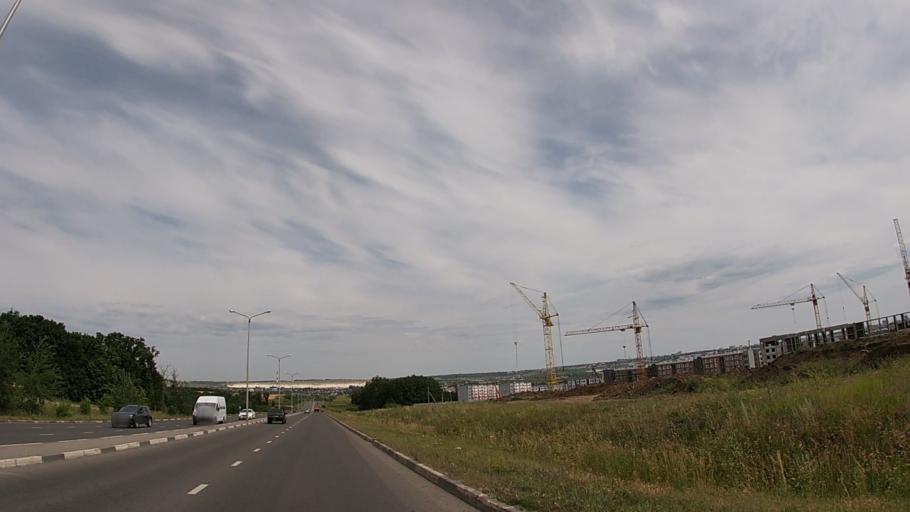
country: RU
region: Belgorod
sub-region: Belgorodskiy Rayon
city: Belgorod
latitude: 50.5953
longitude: 36.5308
